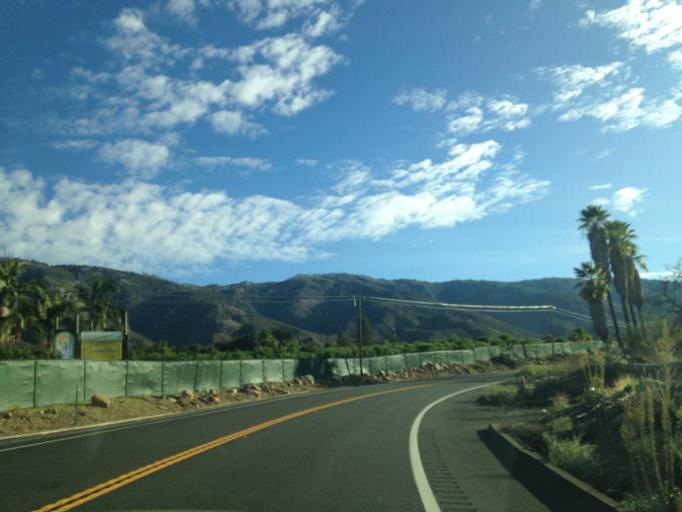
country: US
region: California
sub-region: San Diego County
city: Valley Center
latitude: 33.3019
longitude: -116.9389
